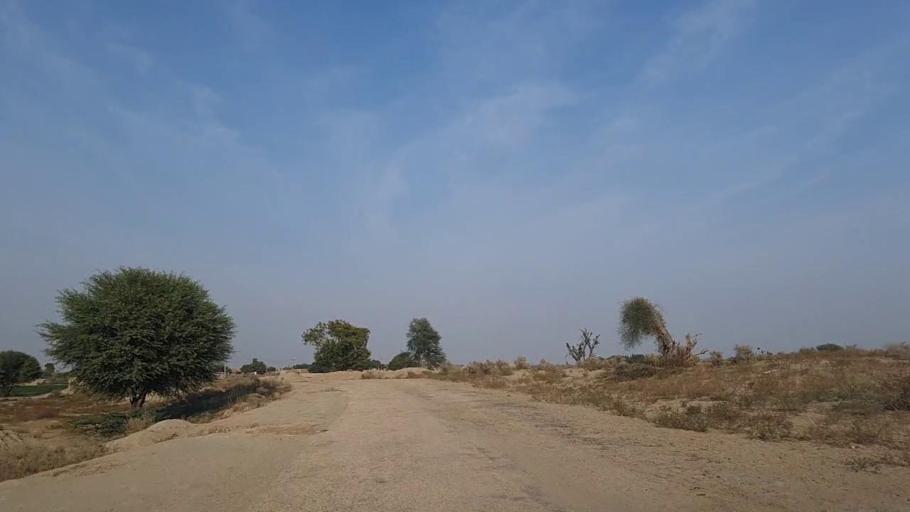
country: PK
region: Sindh
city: Jam Sahib
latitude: 26.4510
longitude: 68.5872
